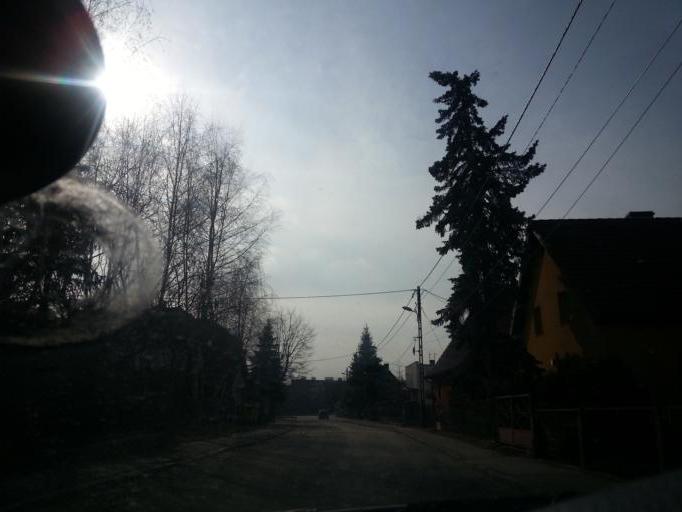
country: PL
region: Lower Silesian Voivodeship
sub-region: Powiat jeleniogorski
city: Jezow Sudecki
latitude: 50.9137
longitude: 15.7459
